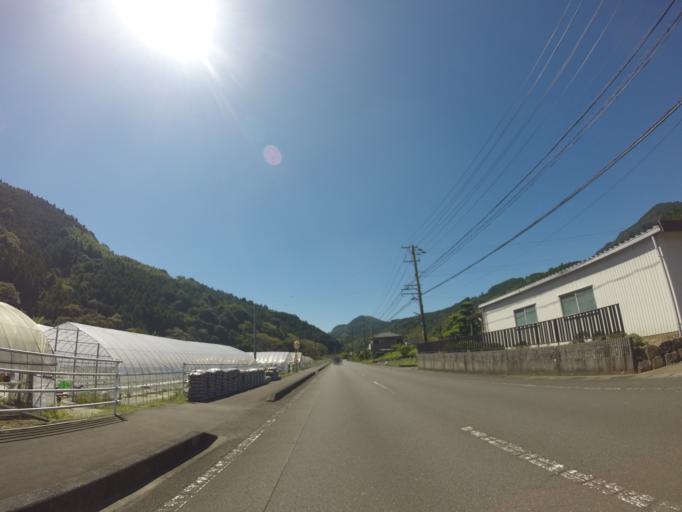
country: JP
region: Shizuoka
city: Fujieda
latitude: 34.9386
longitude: 138.2090
